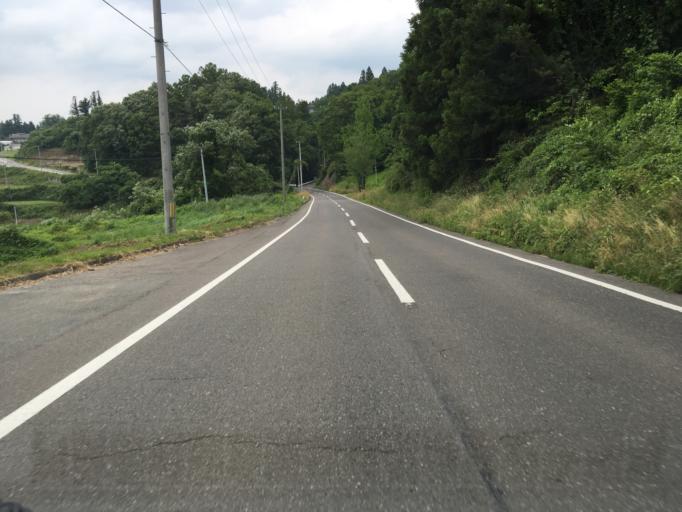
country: JP
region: Fukushima
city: Nihommatsu
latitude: 37.6272
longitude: 140.5397
